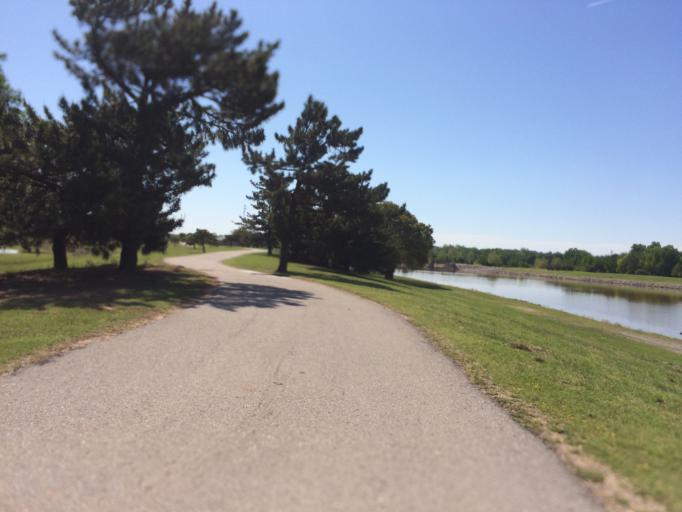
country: US
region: Oklahoma
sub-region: Oklahoma County
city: Oklahoma City
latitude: 35.4515
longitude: -97.5272
